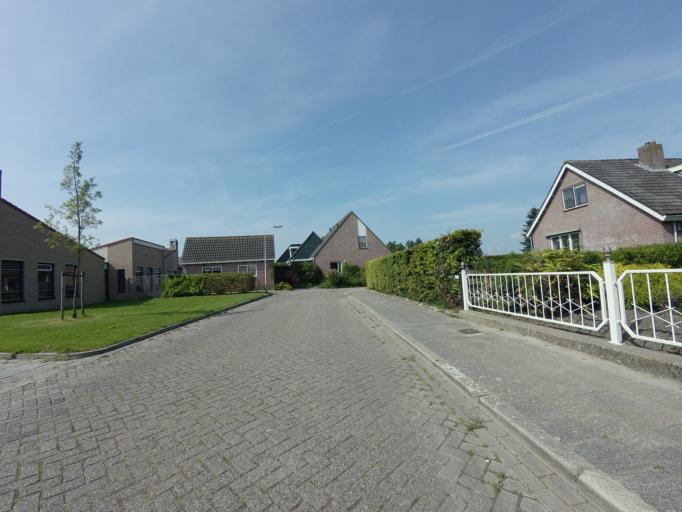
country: NL
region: Friesland
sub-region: Gemeente Lemsterland
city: Echtenerbrug
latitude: 52.8735
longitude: 5.8192
